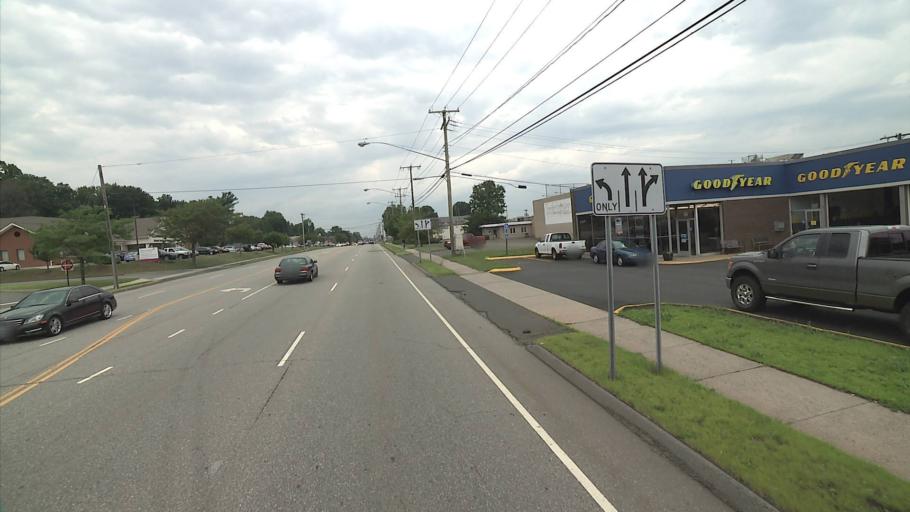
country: US
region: Connecticut
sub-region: Hartford County
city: Wethersfield
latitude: 41.6945
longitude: -72.6569
